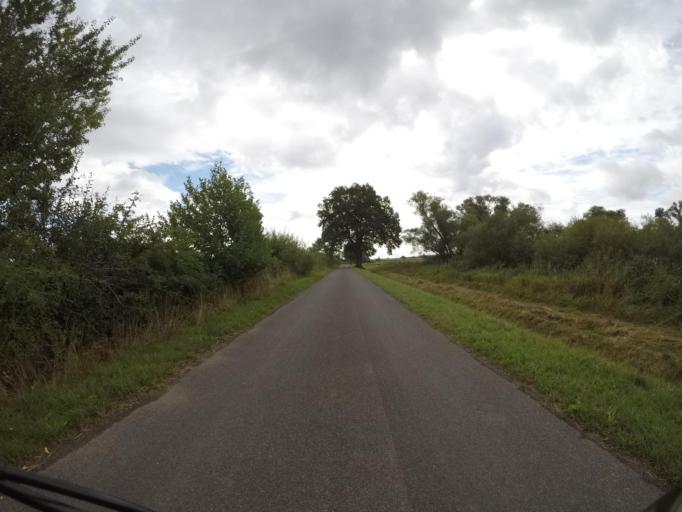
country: DE
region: Lower Saxony
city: Neu Darchau
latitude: 53.2650
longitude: 10.8421
